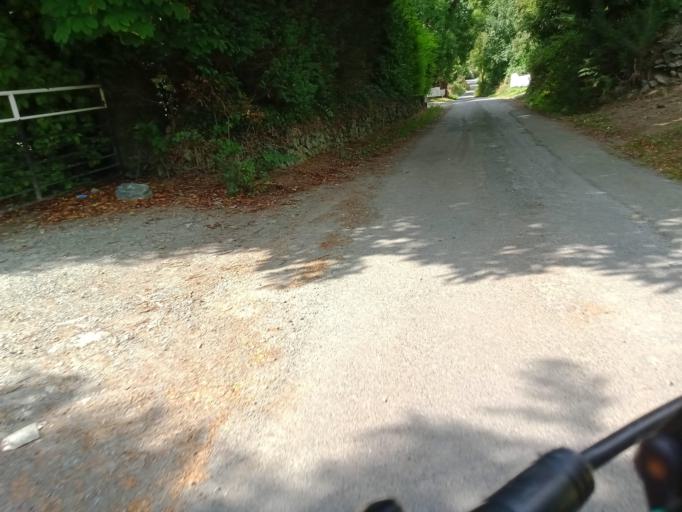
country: IE
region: Munster
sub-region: Waterford
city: Dungarvan
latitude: 52.1363
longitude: -7.4749
